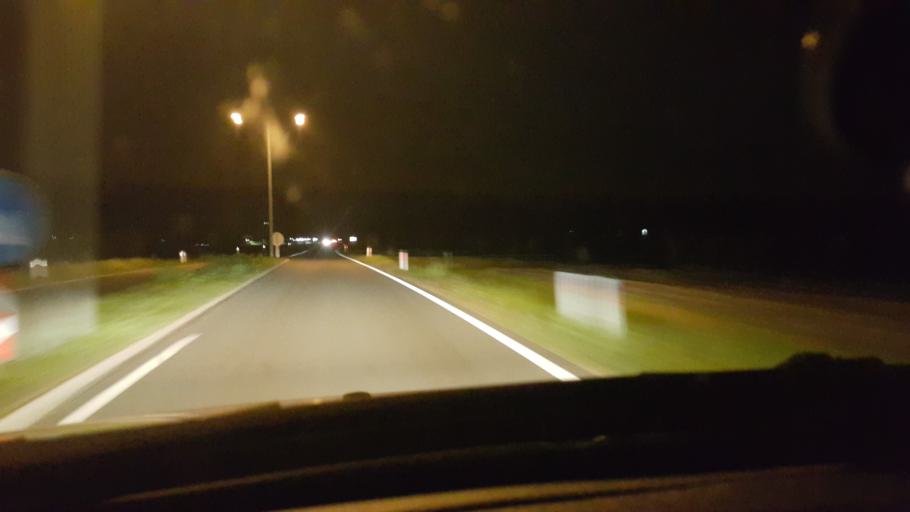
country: AT
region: Styria
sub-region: Politischer Bezirk Deutschlandsberg
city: Sankt Martin im Sulmtal
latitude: 46.7489
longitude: 15.3199
